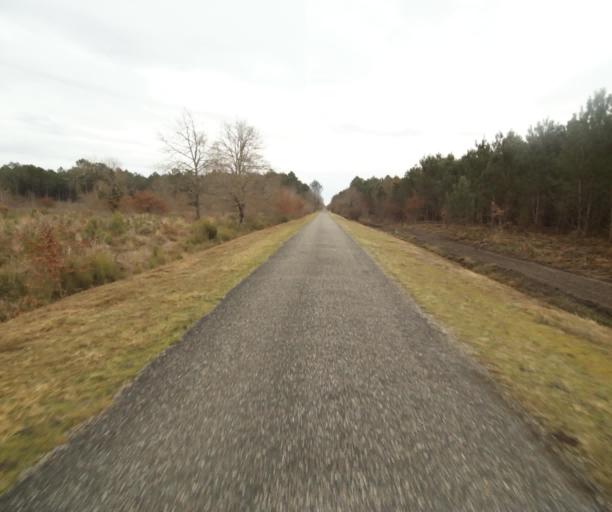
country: FR
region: Aquitaine
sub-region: Departement des Landes
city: Gabarret
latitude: 44.0253
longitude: -0.0521
